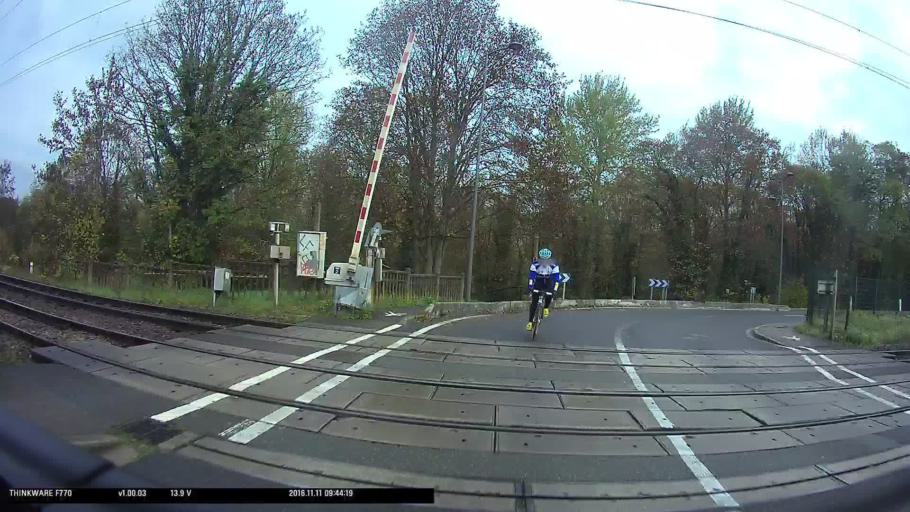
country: FR
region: Ile-de-France
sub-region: Departement du Val-d'Oise
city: Osny
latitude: 49.0643
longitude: 2.0509
